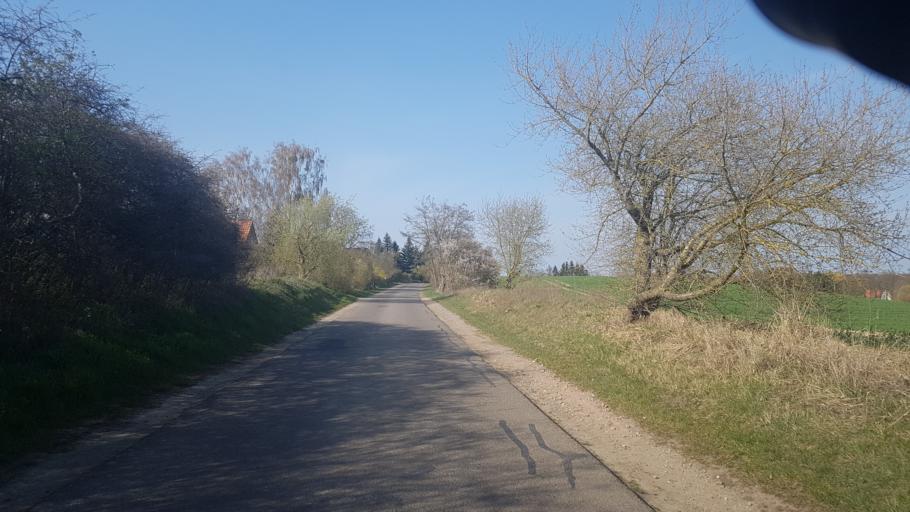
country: DE
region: Brandenburg
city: Gerswalde
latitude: 53.2110
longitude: 13.7857
